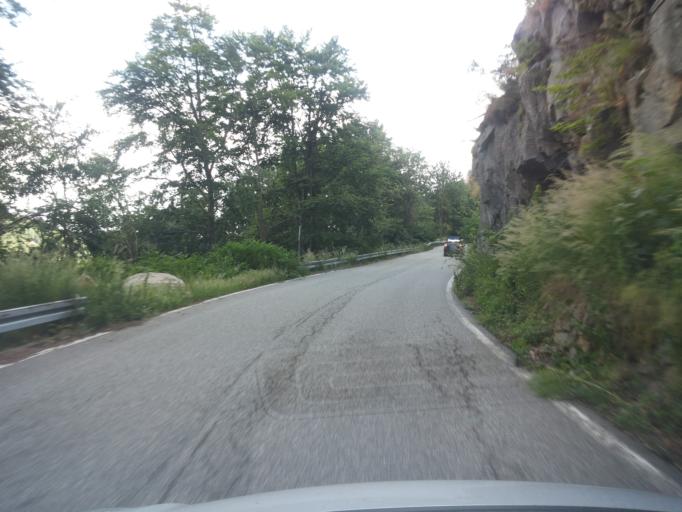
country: IT
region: Piedmont
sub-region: Provincia di Biella
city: Quittengo
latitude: 45.6583
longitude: 8.0213
